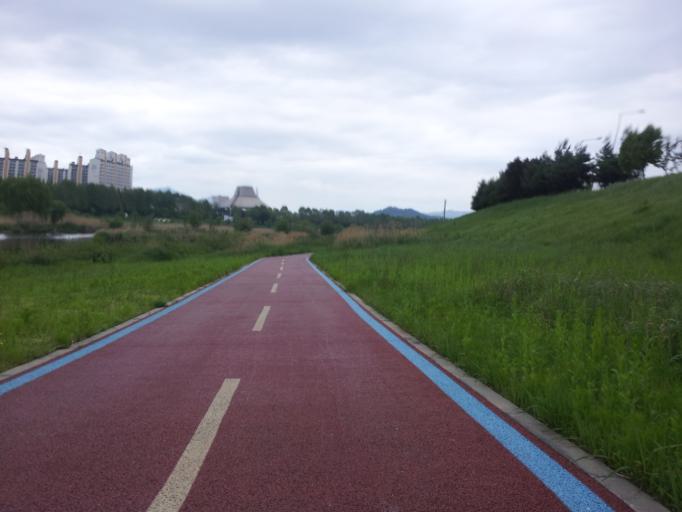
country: KR
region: Daejeon
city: Daejeon
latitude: 36.3630
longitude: 127.3995
